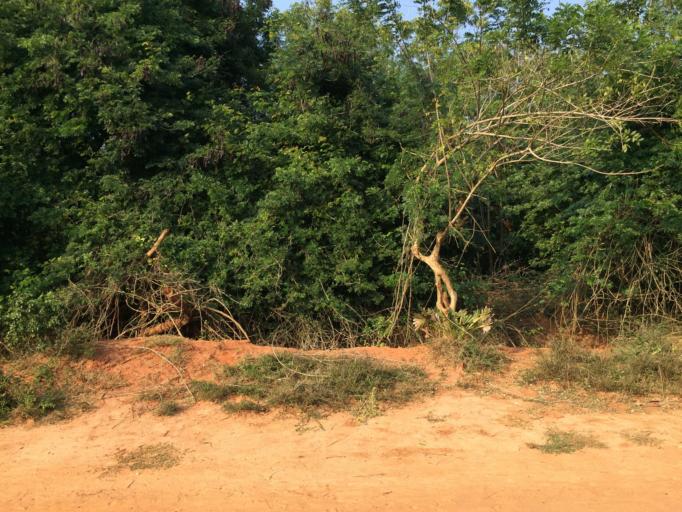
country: IN
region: Tamil Nadu
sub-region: Villupuram
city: Auroville
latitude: 11.9994
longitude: 79.8067
